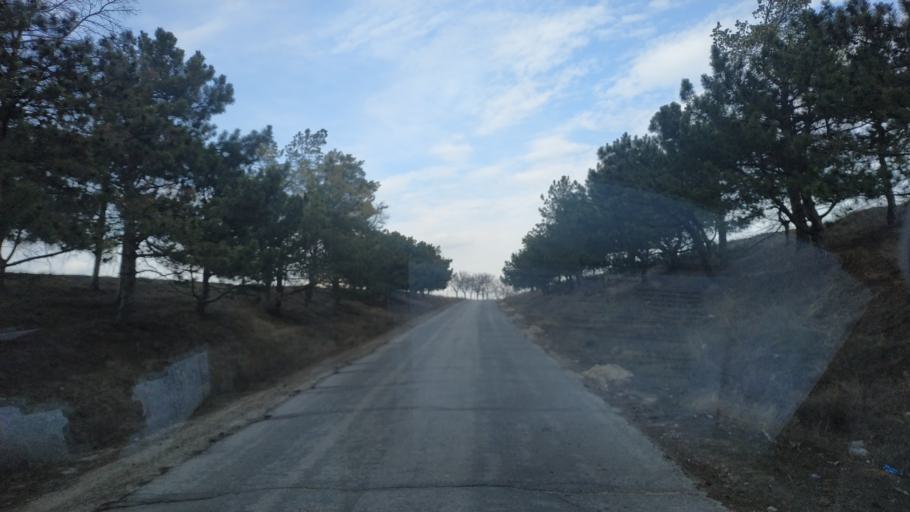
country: MD
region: Anenii Noi
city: Anenii Noi
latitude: 46.9084
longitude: 29.3239
